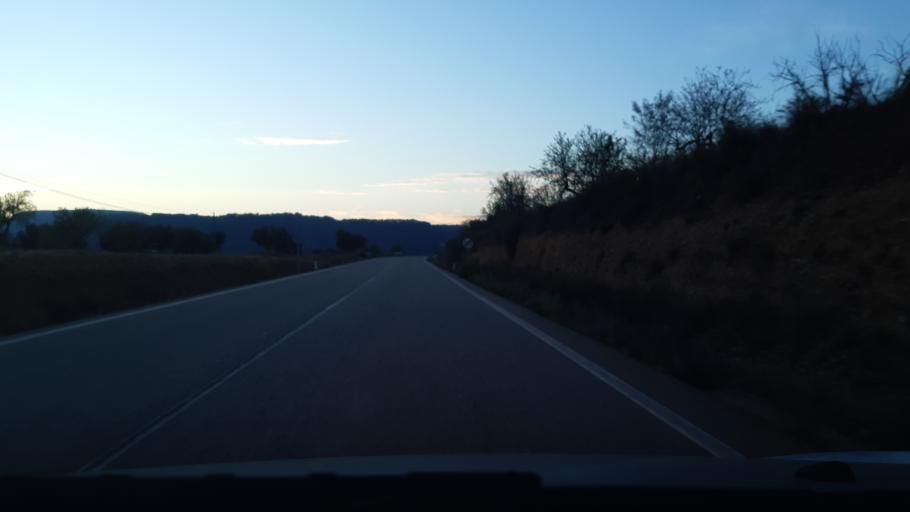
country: ES
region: Aragon
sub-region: Provincia de Teruel
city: Valderrobres
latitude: 40.8638
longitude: 0.1677
